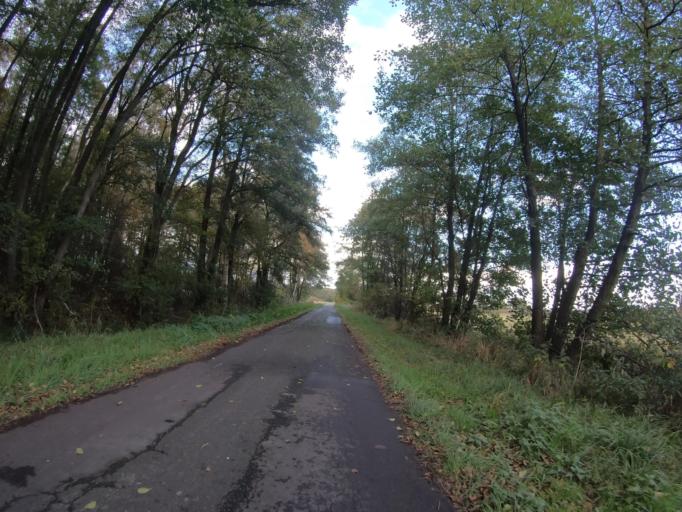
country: DE
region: Lower Saxony
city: Wagenhoff
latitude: 52.5433
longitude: 10.5571
